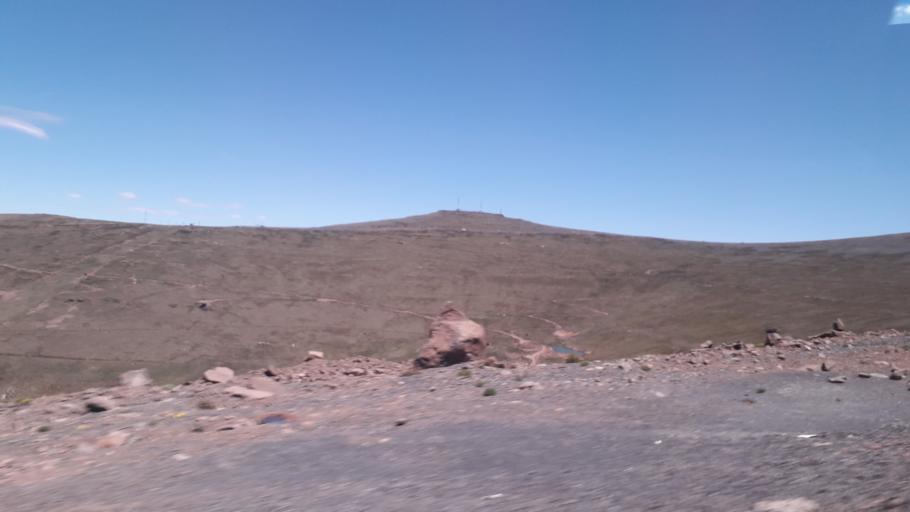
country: ZA
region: Orange Free State
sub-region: Thabo Mofutsanyana District Municipality
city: Phuthaditjhaba
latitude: -28.8227
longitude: 28.7330
